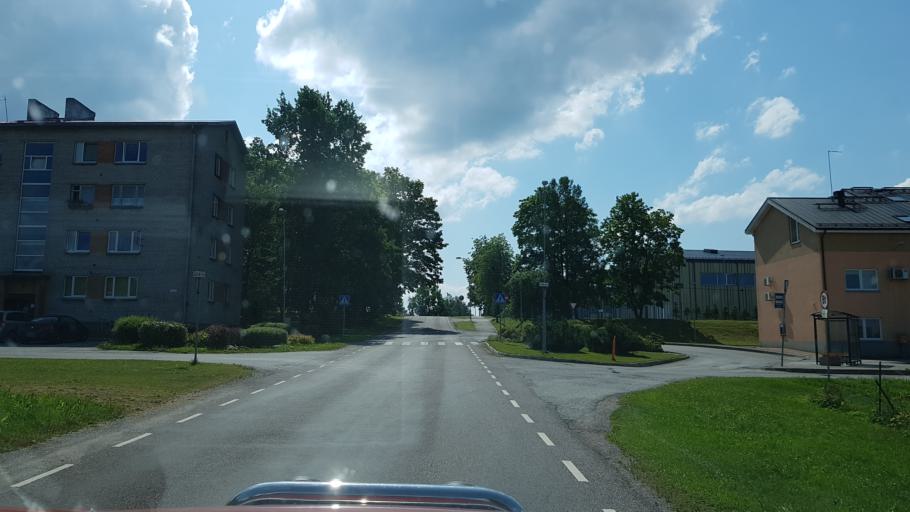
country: EE
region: Ida-Virumaa
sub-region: Sillamaee linn
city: Sillamae
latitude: 59.3754
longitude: 27.8750
